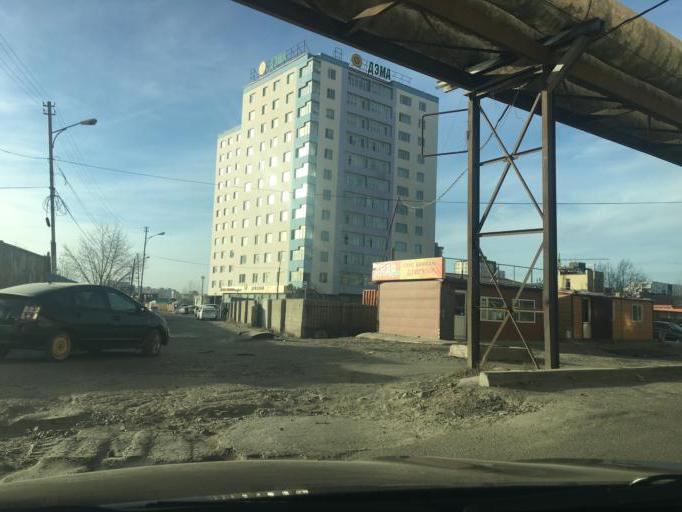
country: MN
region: Ulaanbaatar
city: Ulaanbaatar
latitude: 47.9068
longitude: 106.8930
